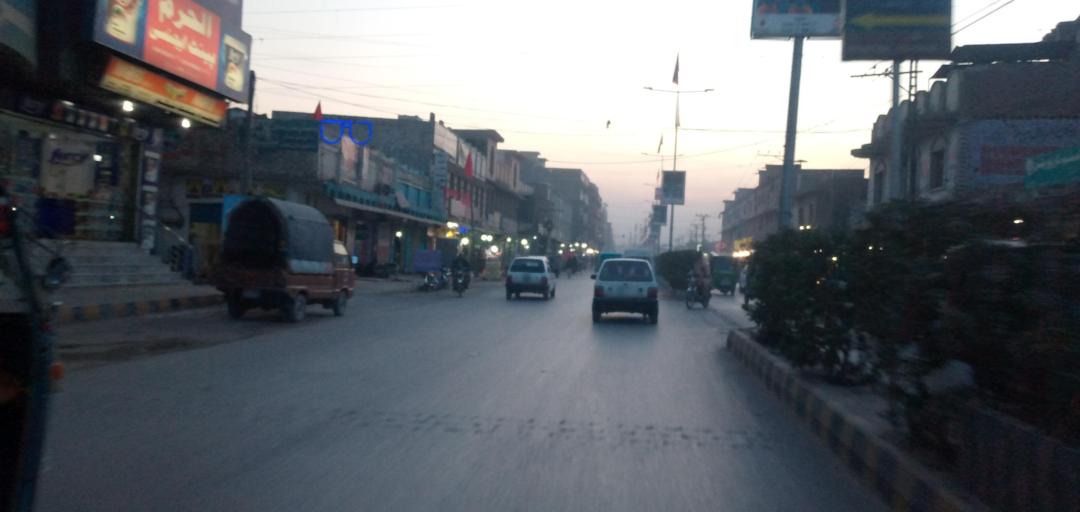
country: PK
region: Khyber Pakhtunkhwa
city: Peshawar
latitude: 34.0299
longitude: 71.6030
